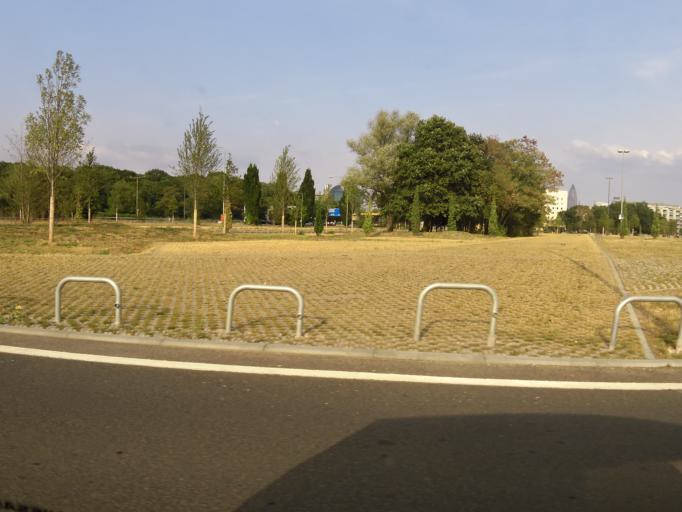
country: DE
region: Hesse
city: Niederrad
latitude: 50.1139
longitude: 8.6143
